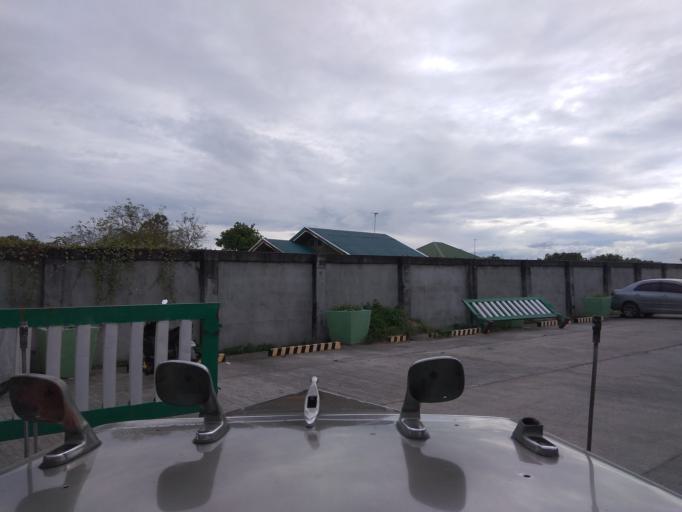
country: PH
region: Central Luzon
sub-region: Province of Pampanga
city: Mexico
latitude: 15.0732
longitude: 120.7196
